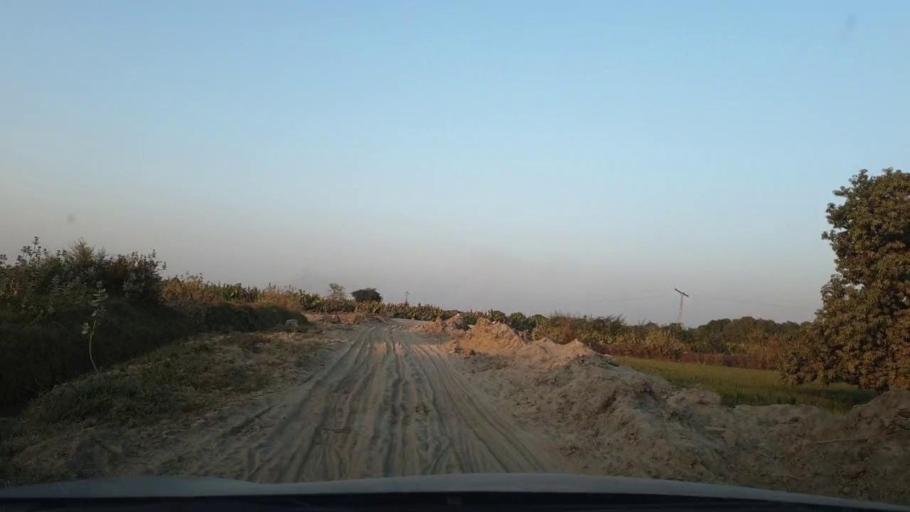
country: PK
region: Sindh
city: Tando Allahyar
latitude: 25.5305
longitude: 68.7366
